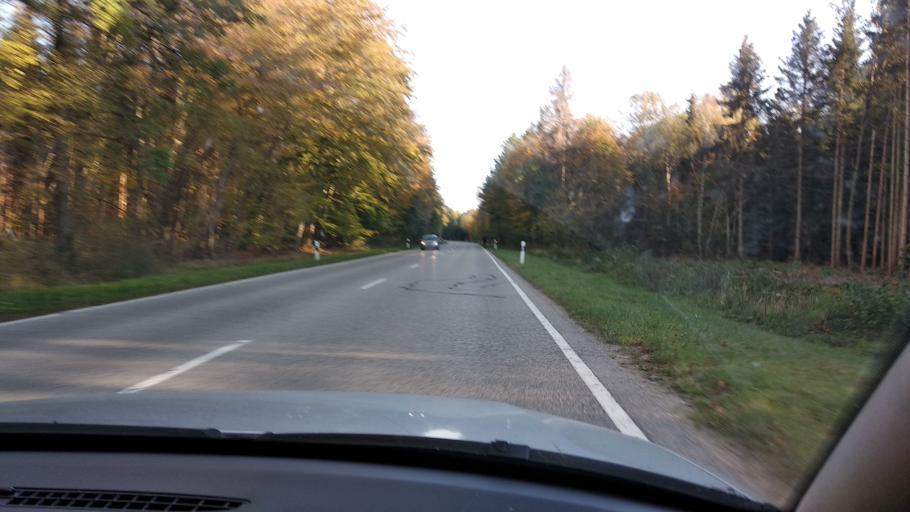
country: DE
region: Bavaria
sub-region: Upper Bavaria
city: Grasbrunn
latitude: 48.0661
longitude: 11.7367
